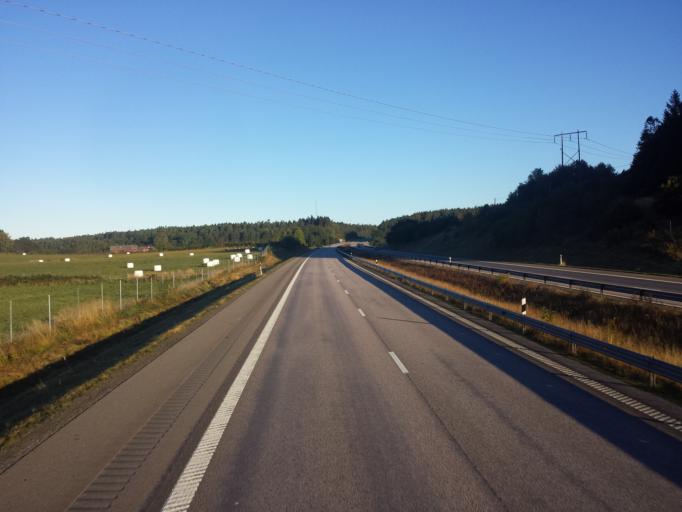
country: SE
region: Halland
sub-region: Varbergs Kommun
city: Varberg
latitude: 57.1831
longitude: 12.2648
